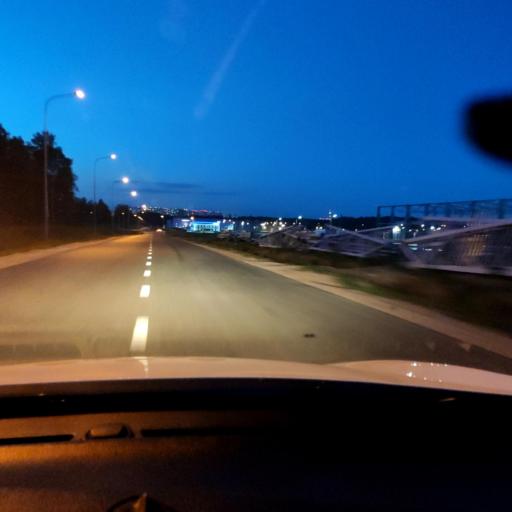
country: RU
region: Tatarstan
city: Osinovo
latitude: 55.8505
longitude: 48.8348
